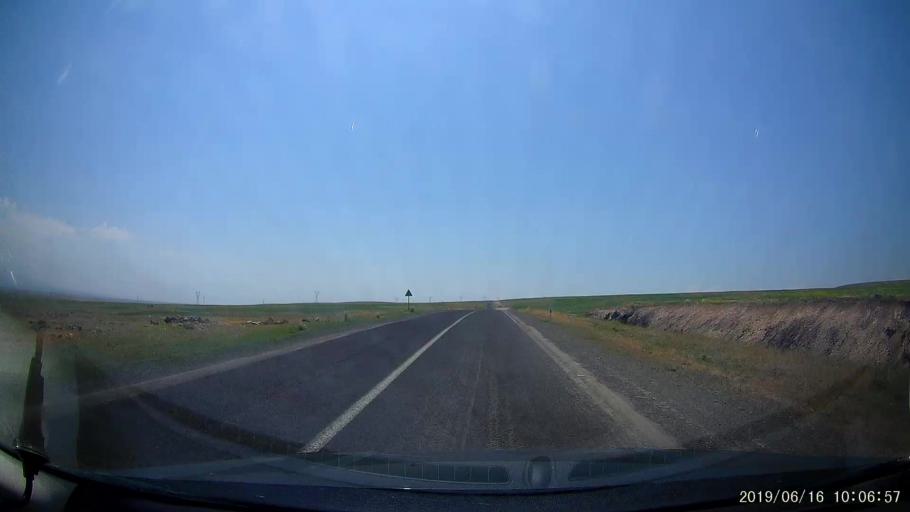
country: TR
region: Kars
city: Digor
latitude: 40.2494
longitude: 43.5491
